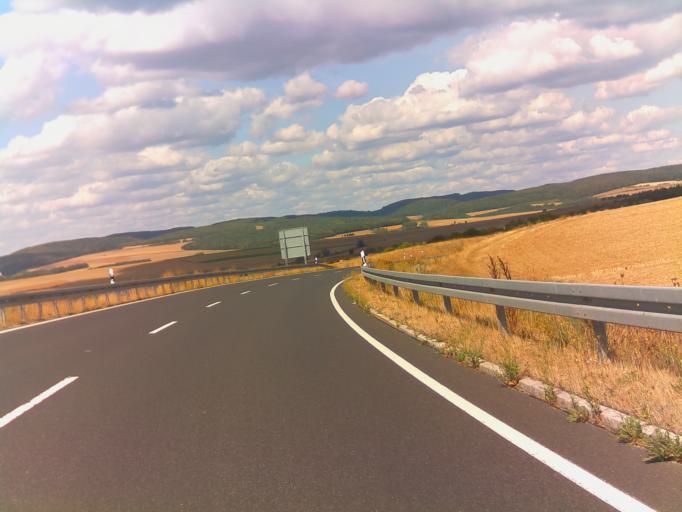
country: DE
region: Bavaria
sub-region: Regierungsbezirk Unterfranken
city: Hendungen
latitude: 50.4155
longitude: 10.3306
